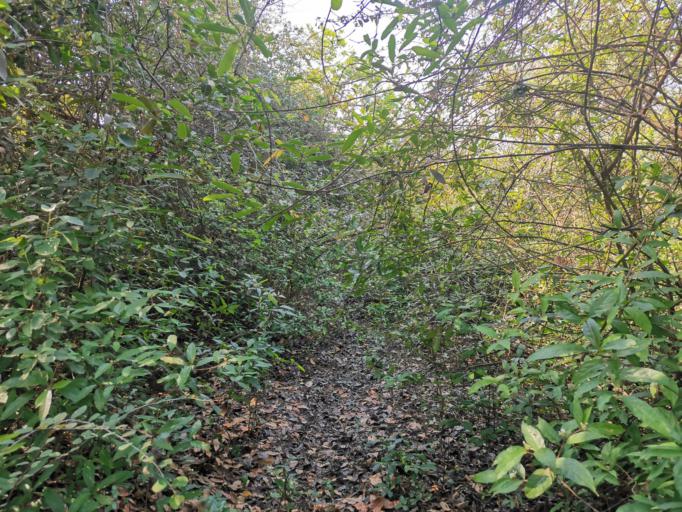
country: KH
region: Battambang
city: Battambang
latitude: 13.3004
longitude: 103.3862
